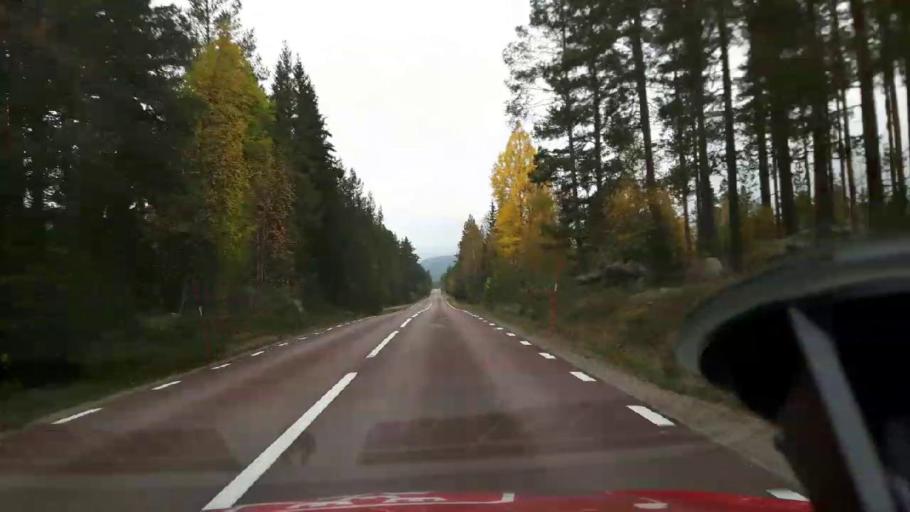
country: SE
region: Jaemtland
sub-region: Harjedalens Kommun
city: Sveg
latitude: 62.3251
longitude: 14.7413
